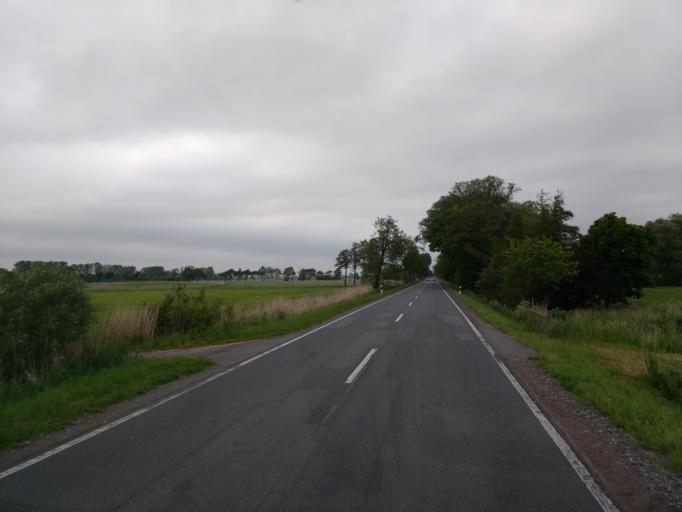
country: DE
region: Lower Saxony
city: Jever
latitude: 53.5982
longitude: 7.9210
